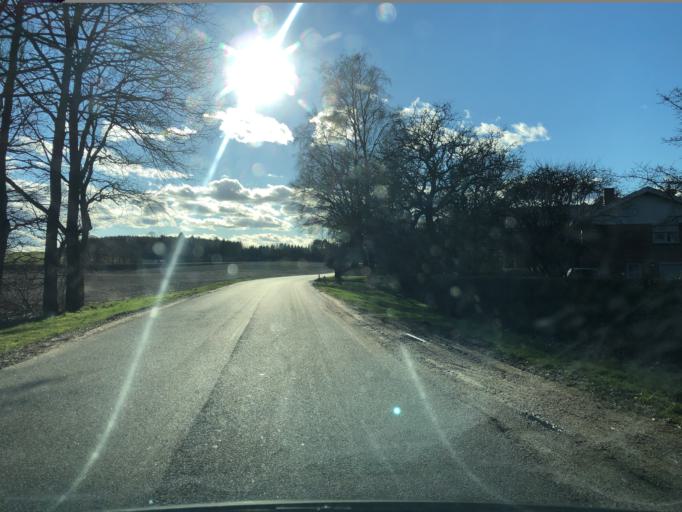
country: DK
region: Central Jutland
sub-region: Silkeborg Kommune
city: Kjellerup
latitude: 56.3465
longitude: 9.5200
